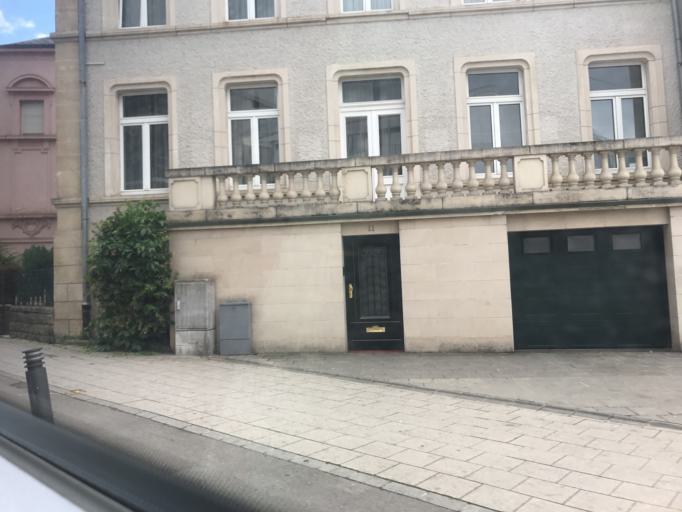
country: LU
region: Luxembourg
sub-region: Canton d'Esch-sur-Alzette
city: Esch-sur-Alzette
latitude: 49.4958
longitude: 5.9867
